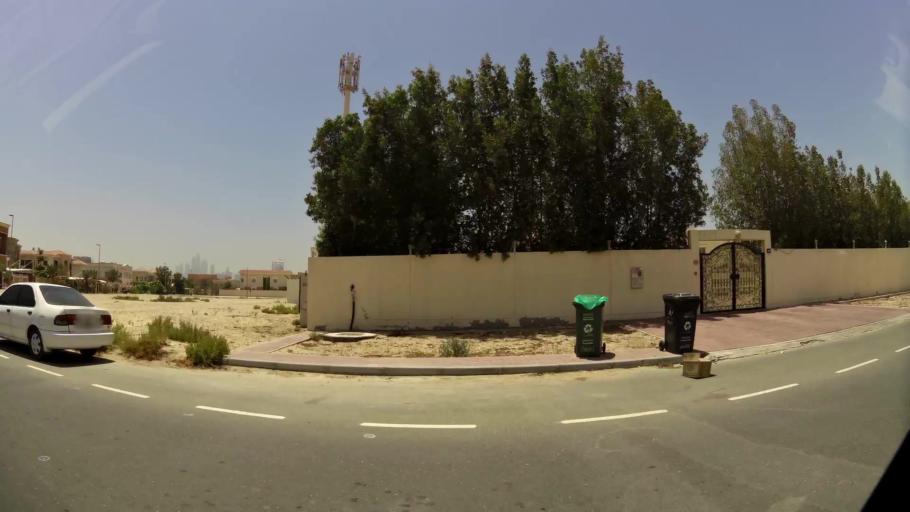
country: AE
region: Dubai
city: Dubai
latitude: 25.0881
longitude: 55.1979
